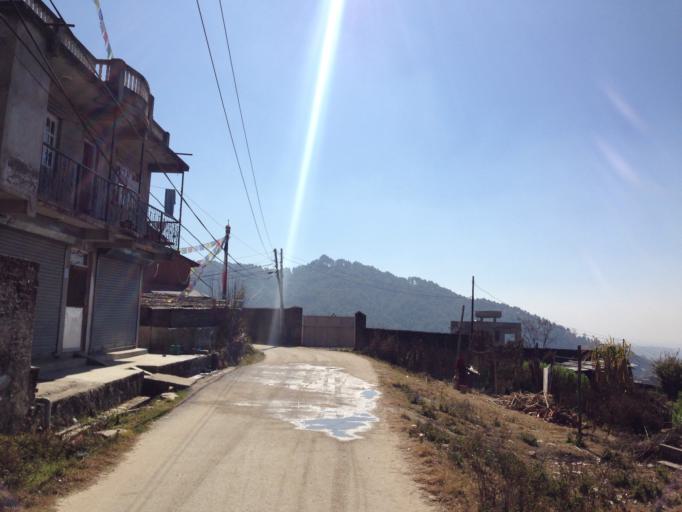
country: NP
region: Central Region
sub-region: Bagmati Zone
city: Kathmandu
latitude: 27.7783
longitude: 85.3677
